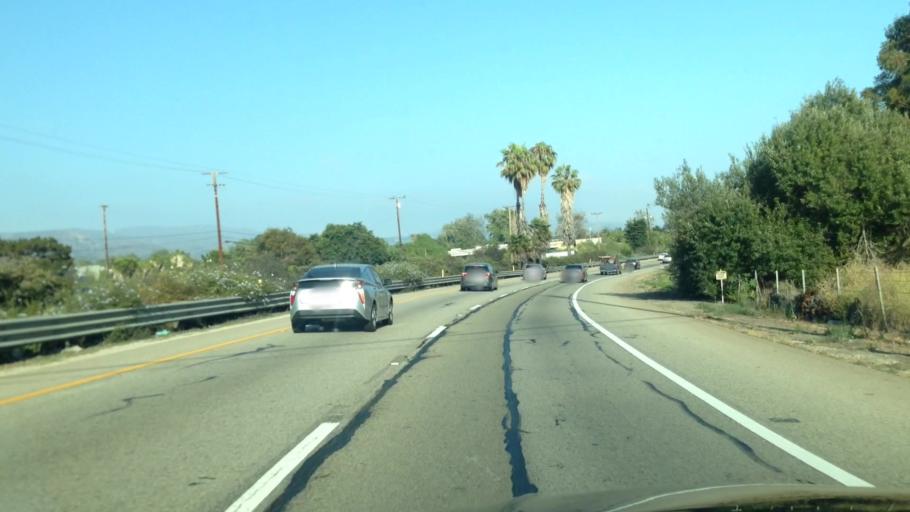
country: US
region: California
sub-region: Santa Barbara County
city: Toro Canyon
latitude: 34.4160
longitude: -119.5605
